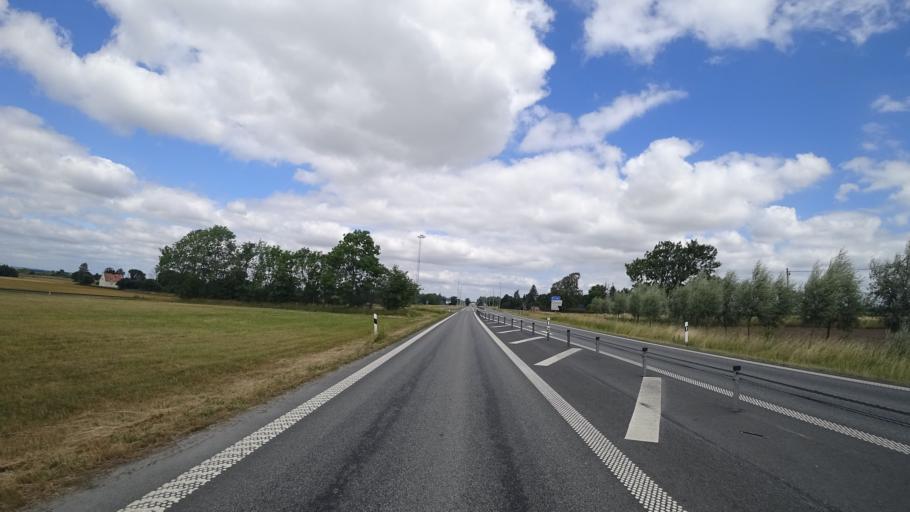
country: SE
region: Skane
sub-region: Kristianstads Kommun
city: Fjalkinge
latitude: 55.9999
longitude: 14.2675
